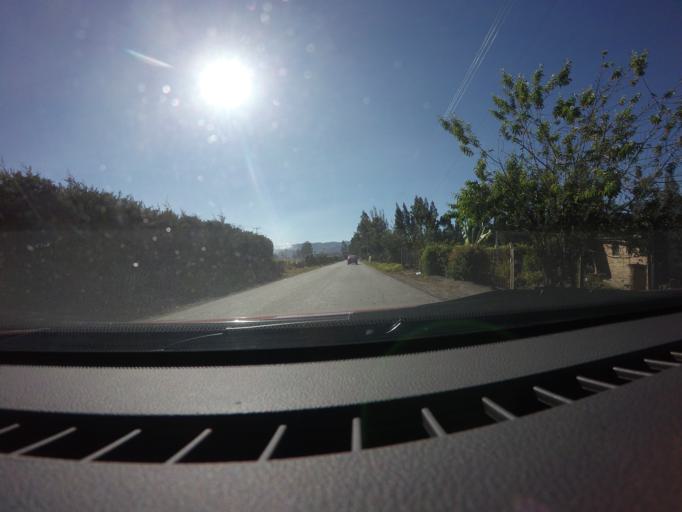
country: CO
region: Cundinamarca
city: Ubate
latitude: 5.2951
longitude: -73.8129
